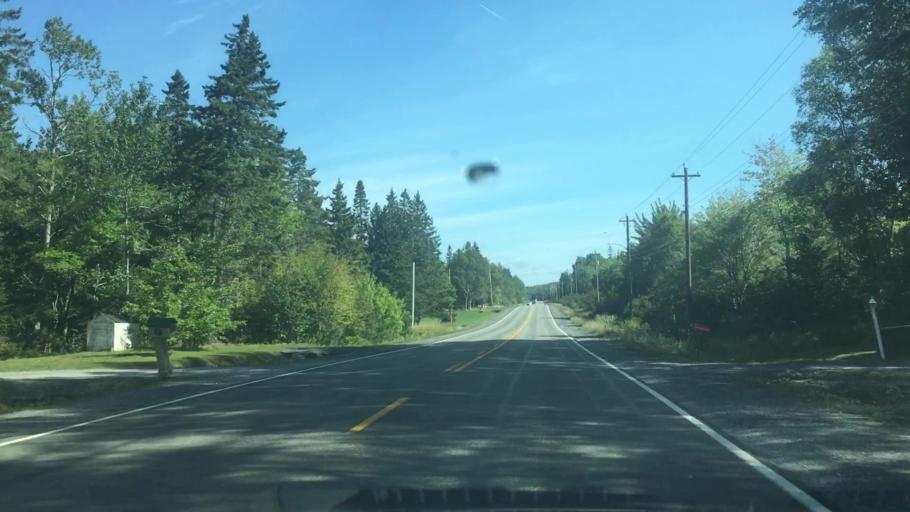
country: CA
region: Nova Scotia
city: Sydney
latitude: 45.9843
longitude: -60.4216
